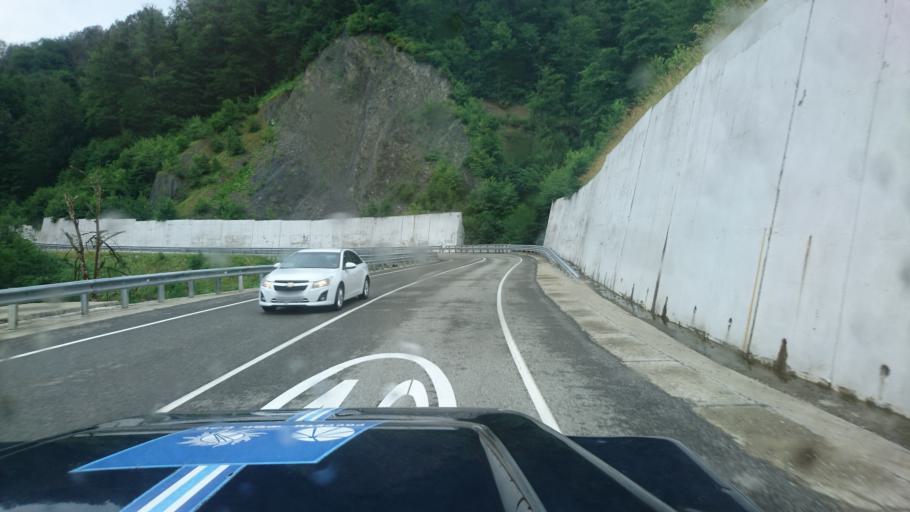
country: RU
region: Krasnodarskiy
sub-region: Sochi City
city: Krasnaya Polyana
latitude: 43.6669
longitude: 40.2927
